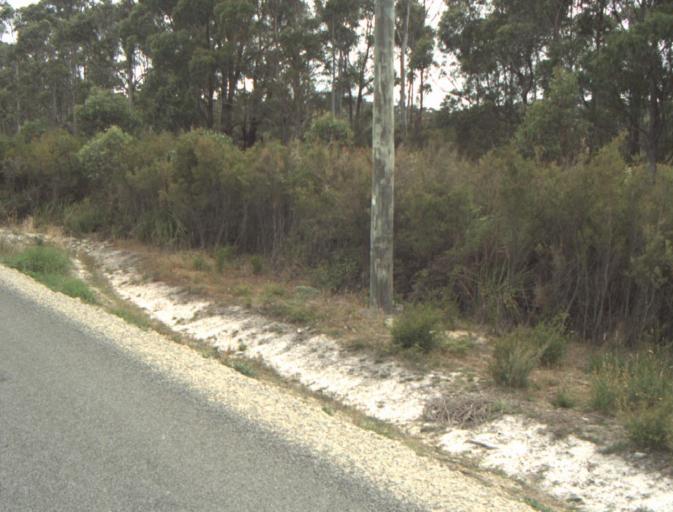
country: AU
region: Tasmania
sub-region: Launceston
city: Mayfield
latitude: -41.2125
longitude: 147.1895
